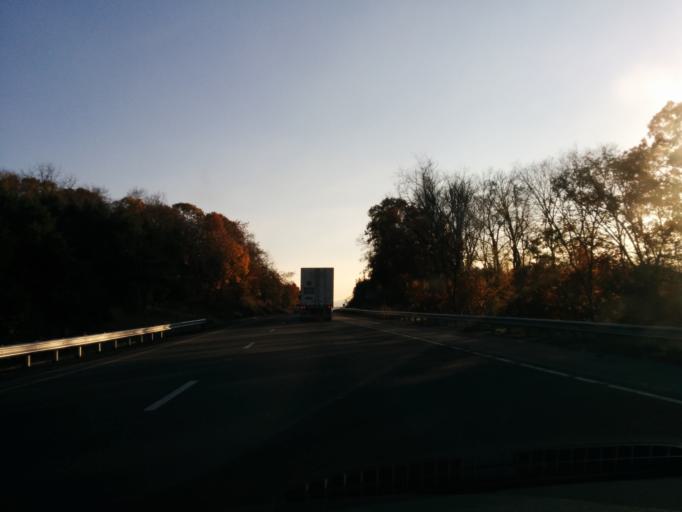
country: US
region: Virginia
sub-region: Rockbridge County
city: East Lexington
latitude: 37.8344
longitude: -79.3708
